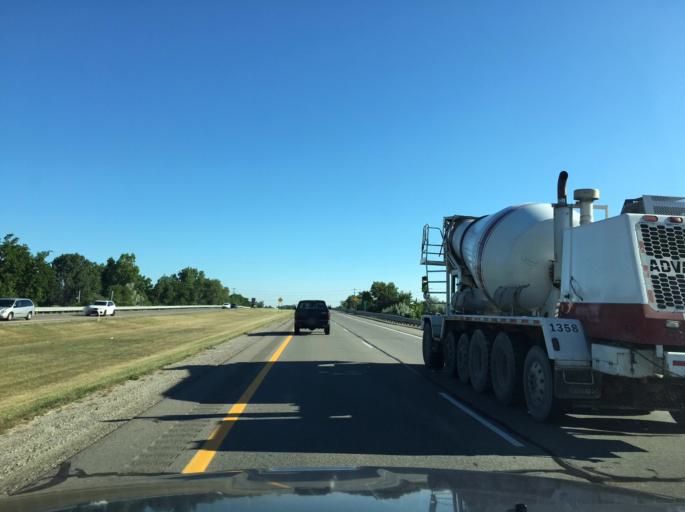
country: US
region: Michigan
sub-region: Macomb County
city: Utica
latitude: 42.6167
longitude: -83.0120
